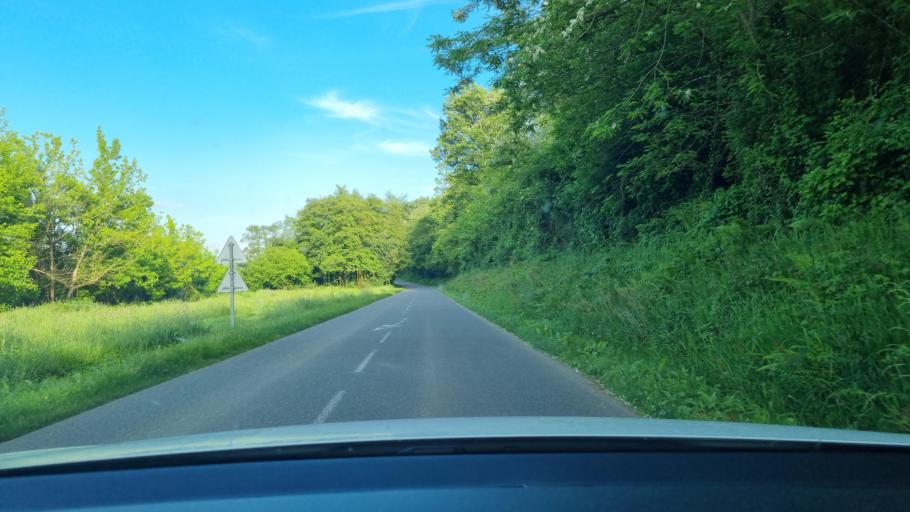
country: FR
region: Aquitaine
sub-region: Departement des Landes
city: Peyrehorade
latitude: 43.5370
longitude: -1.1578
